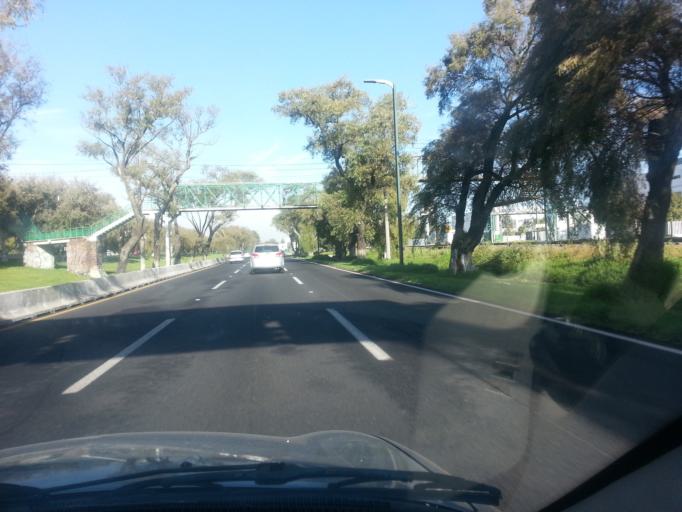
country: MX
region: Mexico
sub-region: San Mateo Atenco
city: Santa Maria la Asuncion
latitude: 19.2861
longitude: -99.5425
